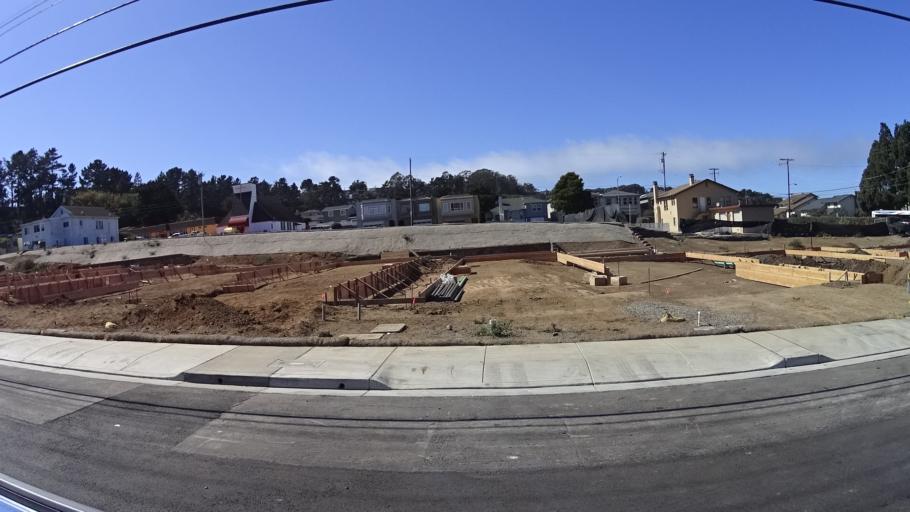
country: US
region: California
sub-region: San Mateo County
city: Broadmoor
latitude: 37.6873
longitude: -122.4743
